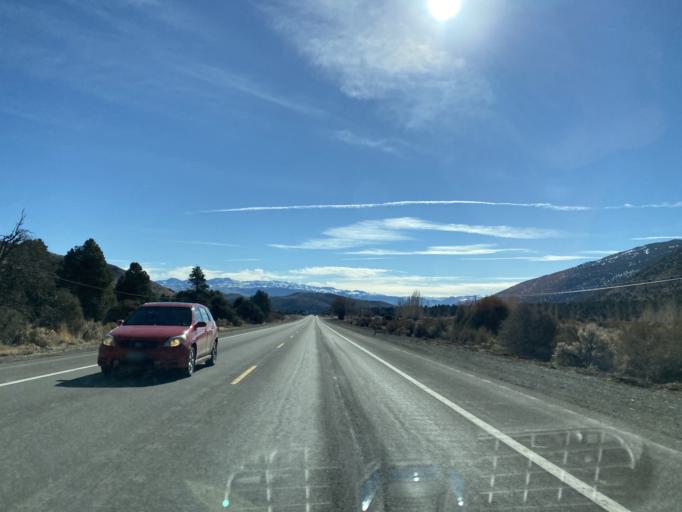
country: US
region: Nevada
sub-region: Douglas County
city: Gardnerville Ranchos
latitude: 38.7513
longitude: -119.5699
